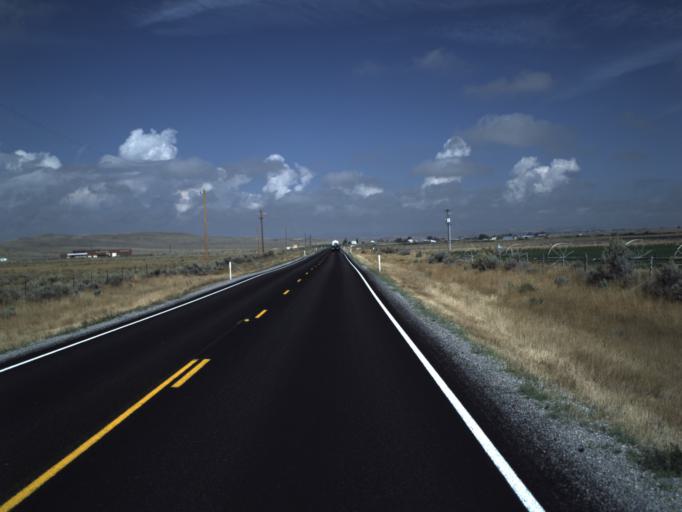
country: US
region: Utah
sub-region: Rich County
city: Randolph
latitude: 41.5820
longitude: -111.1663
